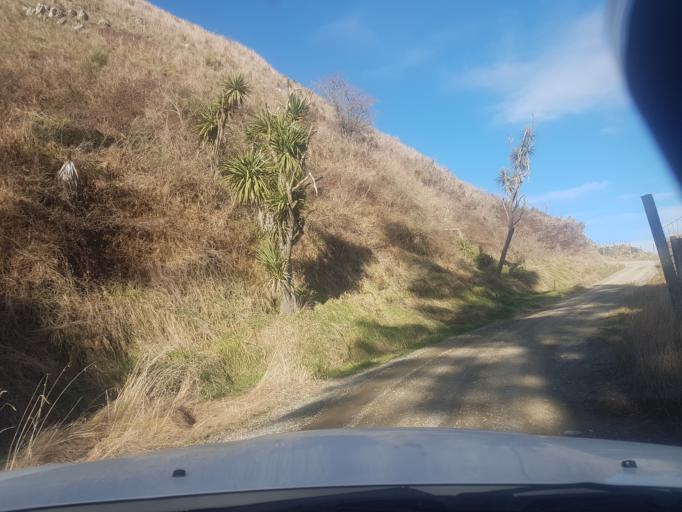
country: NZ
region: Canterbury
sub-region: Timaru District
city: Pleasant Point
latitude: -44.1686
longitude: 170.8820
